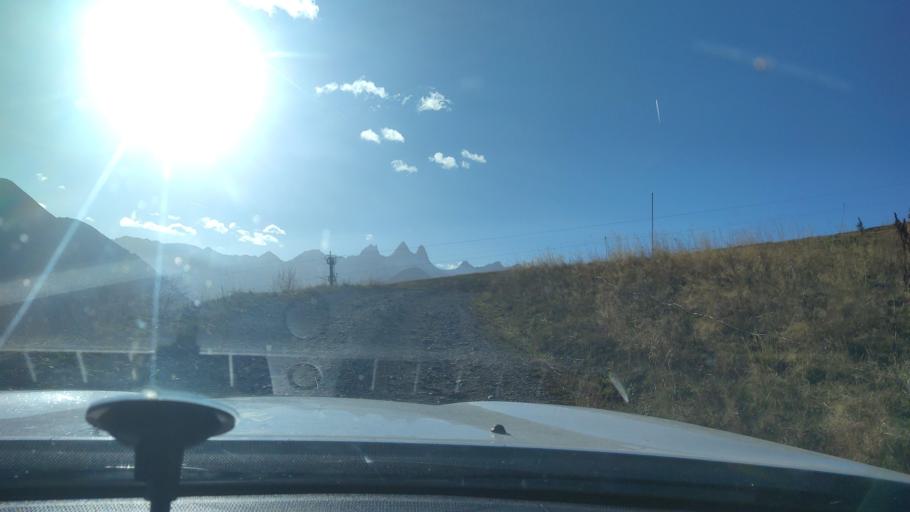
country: FR
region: Rhone-Alpes
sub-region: Departement de la Savoie
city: Saint-Jean-de-Maurienne
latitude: 45.2296
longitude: 6.2575
